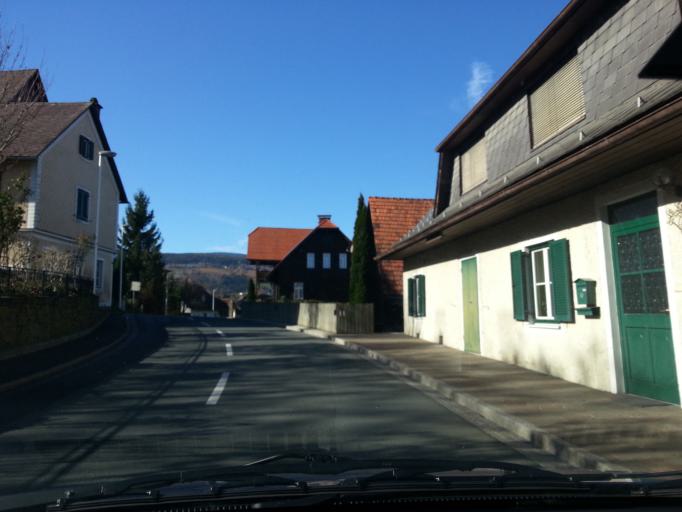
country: AT
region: Styria
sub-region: Politischer Bezirk Deutschlandsberg
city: Sankt Stefan ob Stainz
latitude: 46.9298
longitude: 15.2533
